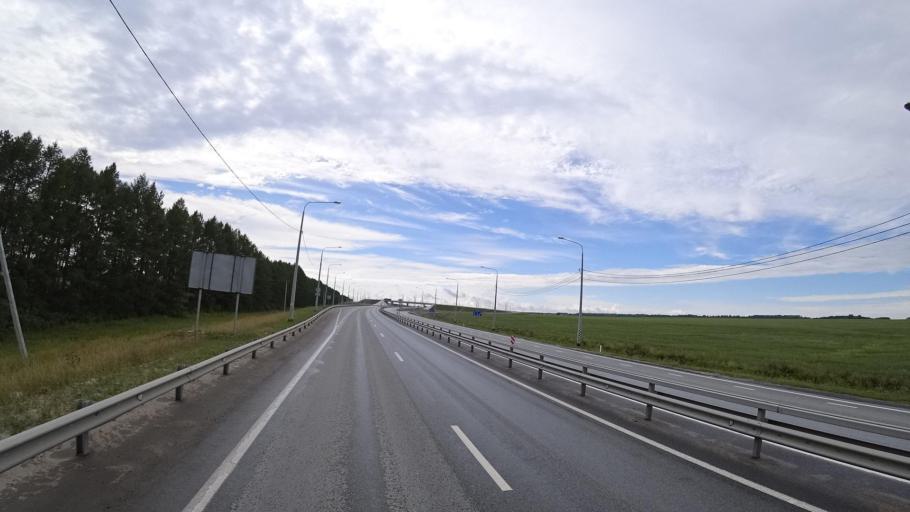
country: RU
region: Sverdlovsk
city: Kamyshlov
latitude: 56.8485
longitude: 62.8459
